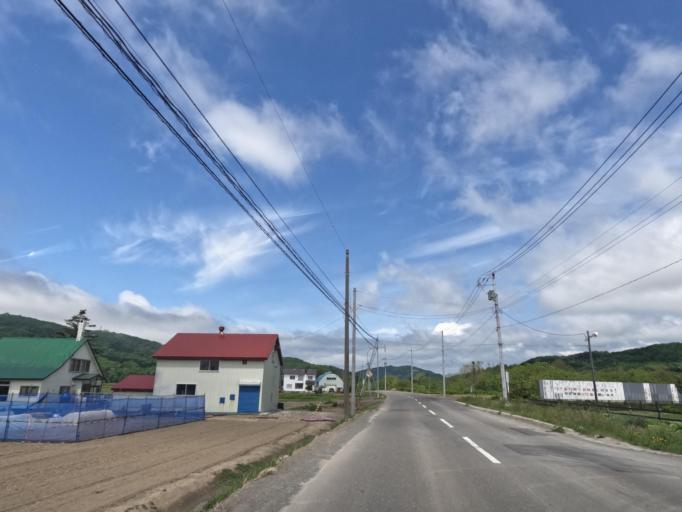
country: JP
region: Hokkaido
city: Tobetsu
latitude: 43.2804
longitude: 141.5355
